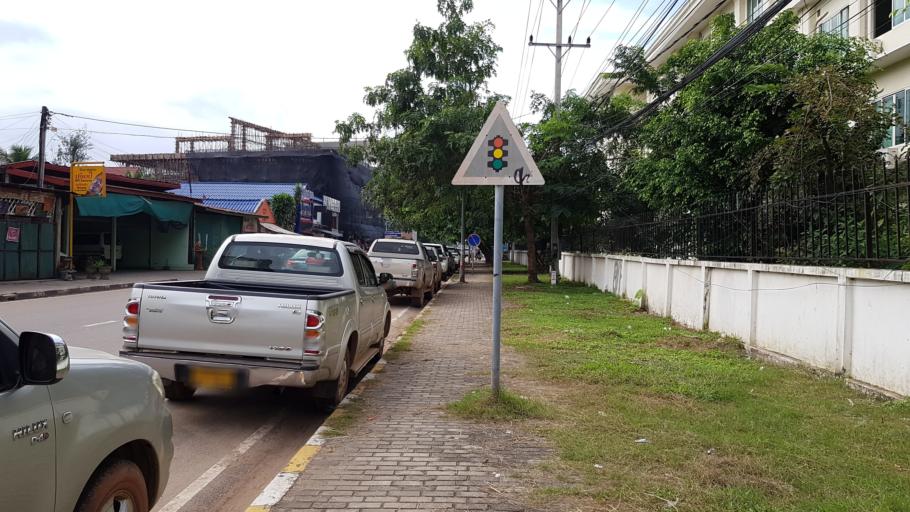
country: LA
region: Vientiane
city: Vientiane
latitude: 17.9687
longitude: 102.5990
